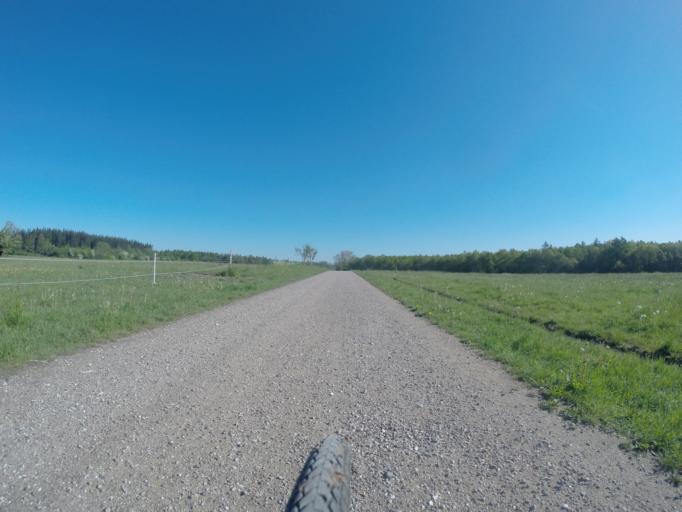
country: DK
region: Capital Region
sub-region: Albertslund Kommune
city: Albertslund
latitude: 55.6927
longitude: 12.3435
